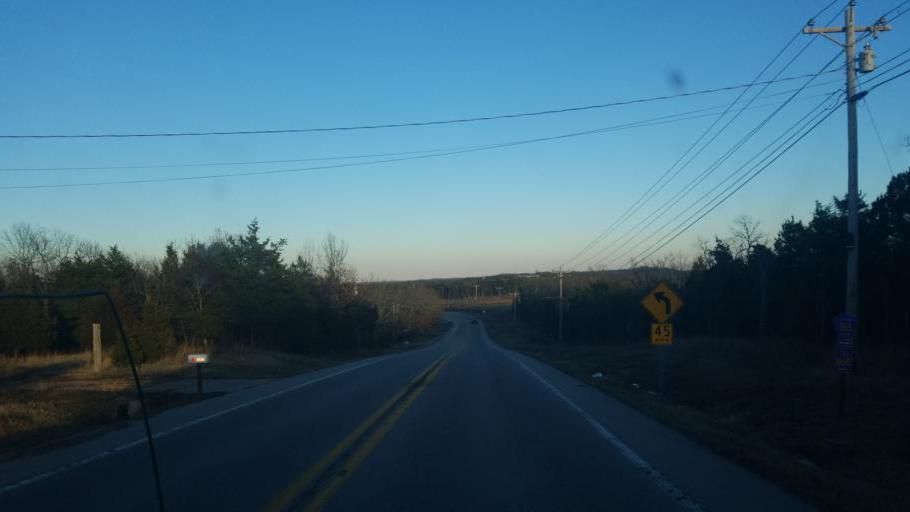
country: US
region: Arkansas
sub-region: Baxter County
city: Mountain Home
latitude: 36.3798
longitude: -92.1965
